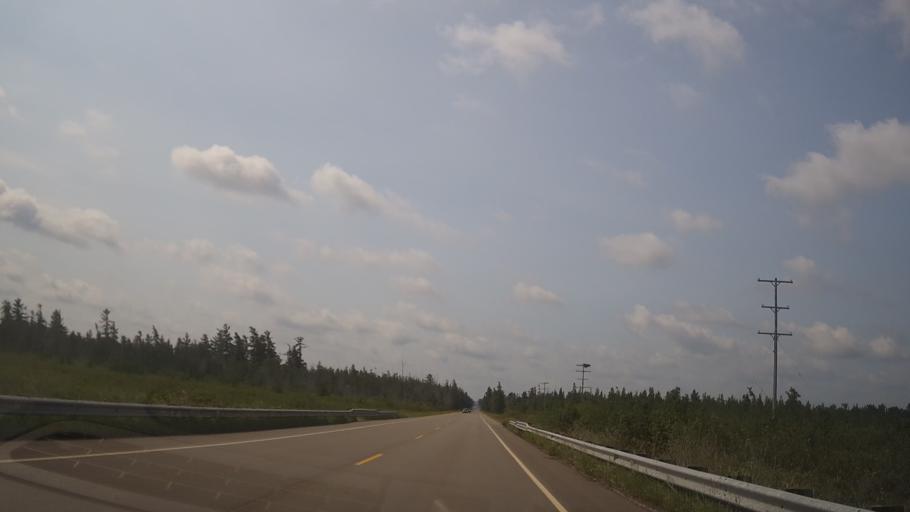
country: US
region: Michigan
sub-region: Roscommon County
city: Saint Helen
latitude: 44.3879
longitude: -84.4103
